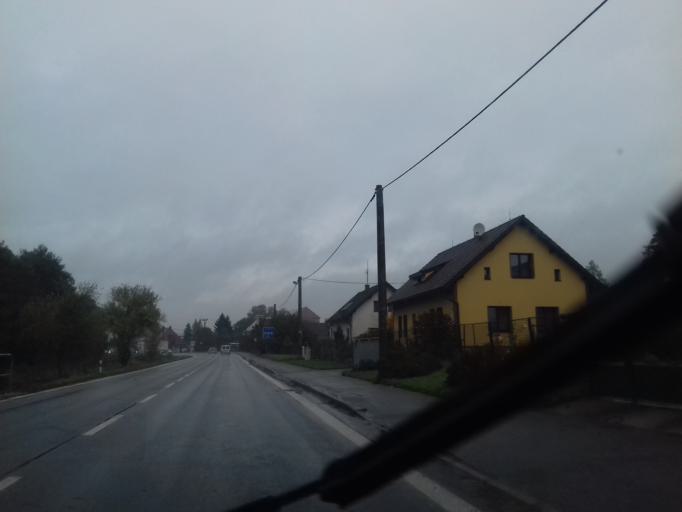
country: CZ
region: Liberecky
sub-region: Okres Semily
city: Turnov
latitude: 50.5593
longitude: 15.2031
